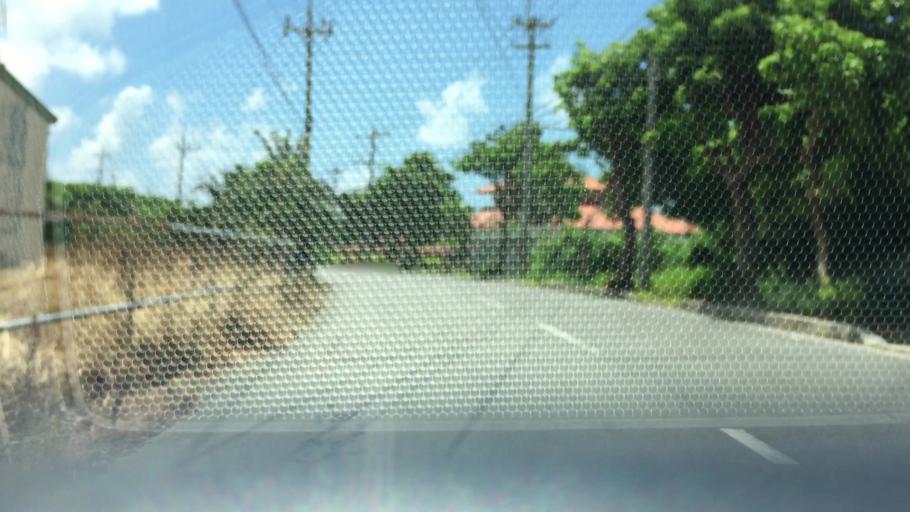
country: JP
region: Okinawa
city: Ishigaki
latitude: 24.3626
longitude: 124.1168
